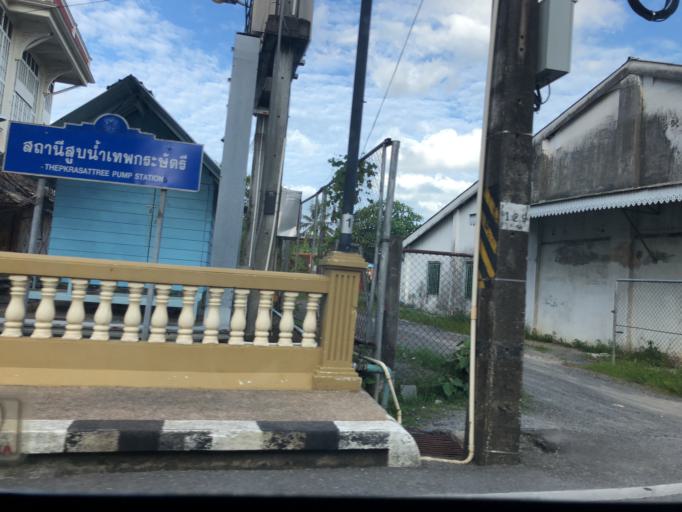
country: TH
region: Phuket
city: Ban Talat Nua
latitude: 7.8866
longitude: 98.3904
